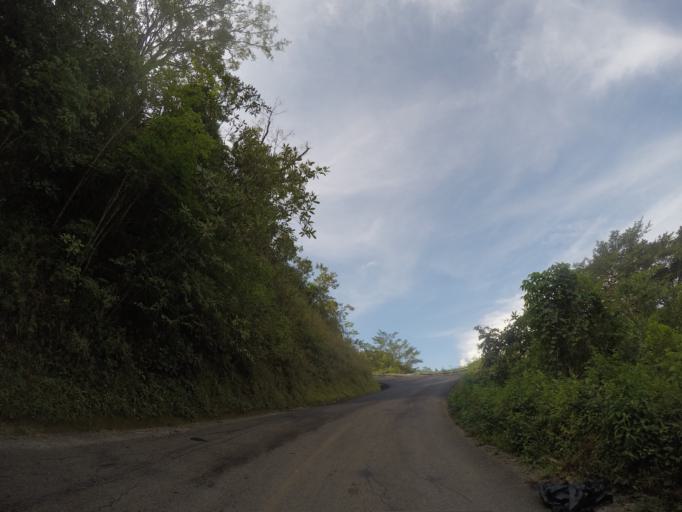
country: MX
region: Oaxaca
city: Pluma Hidalgo
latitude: 15.9335
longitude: -96.4258
